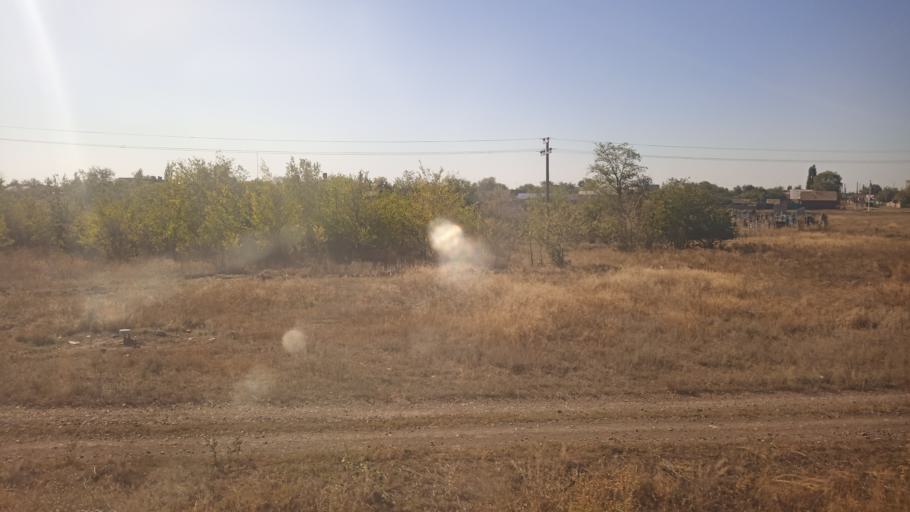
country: RU
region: Saratov
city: Pushkino
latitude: 51.2308
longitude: 46.9854
